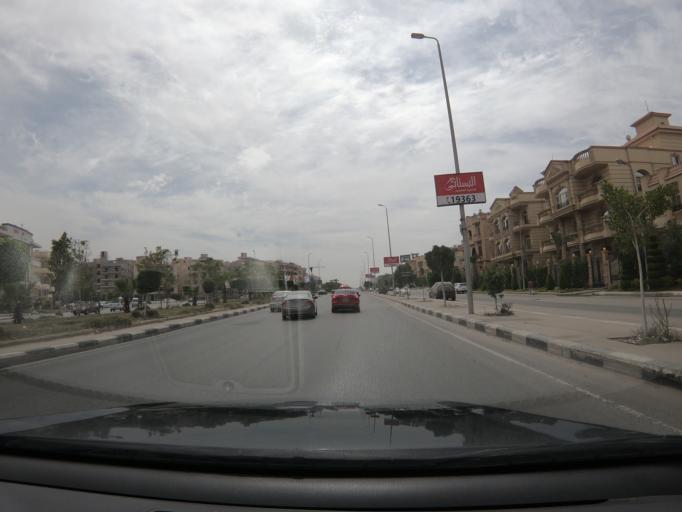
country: EG
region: Muhafazat al Qahirah
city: Cairo
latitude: 30.0087
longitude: 31.4122
